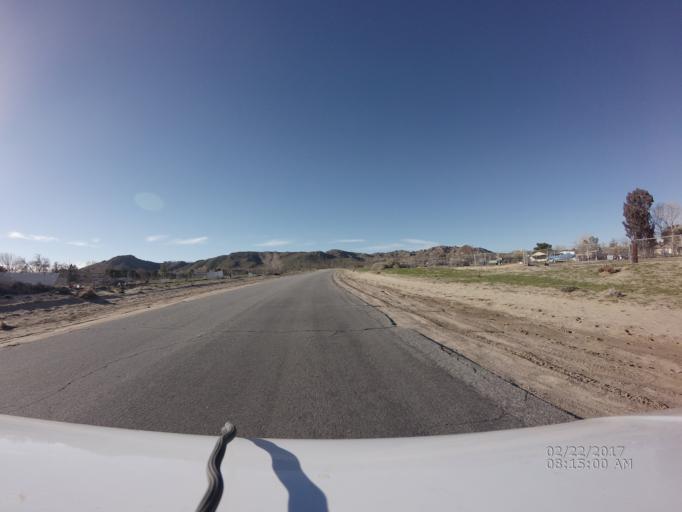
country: US
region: California
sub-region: Los Angeles County
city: Lake Los Angeles
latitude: 34.6194
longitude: -117.8448
